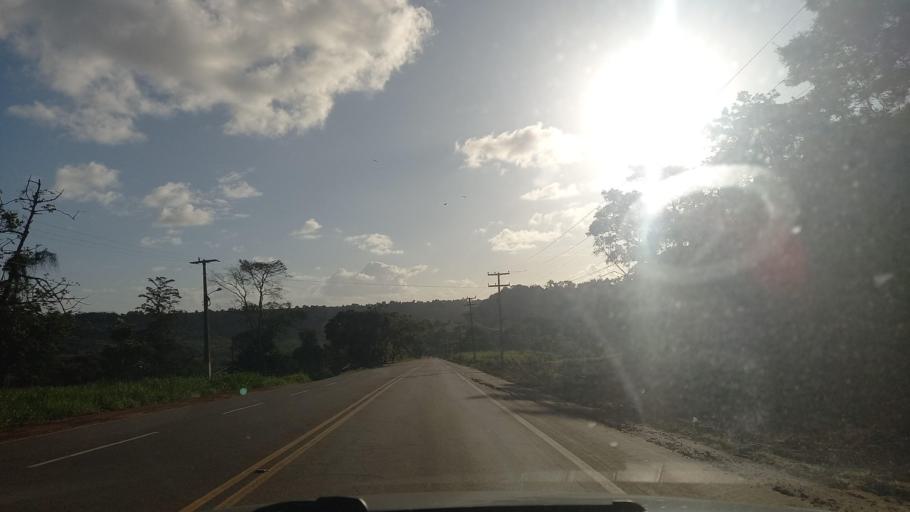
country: BR
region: Alagoas
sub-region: Sao Miguel Dos Campos
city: Sao Miguel dos Campos
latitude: -9.8091
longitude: -36.2133
